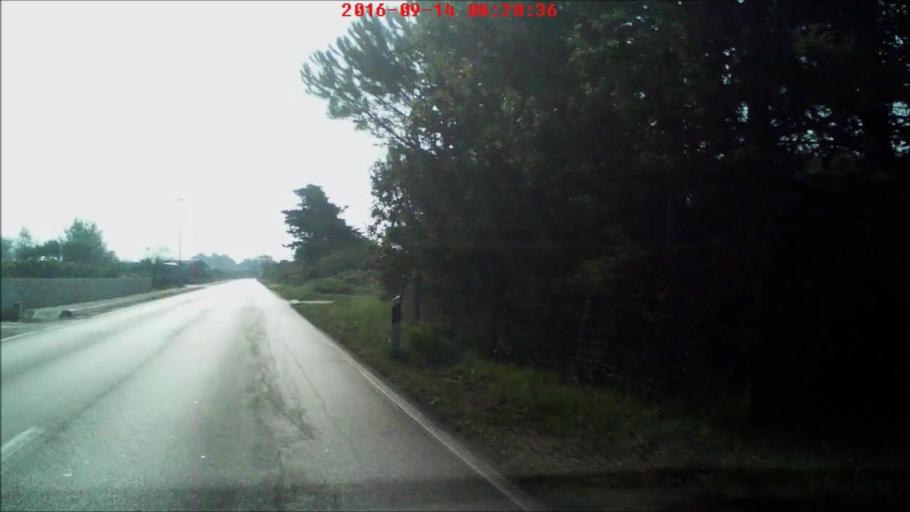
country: HR
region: Zadarska
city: Nin
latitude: 44.2259
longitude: 15.2022
